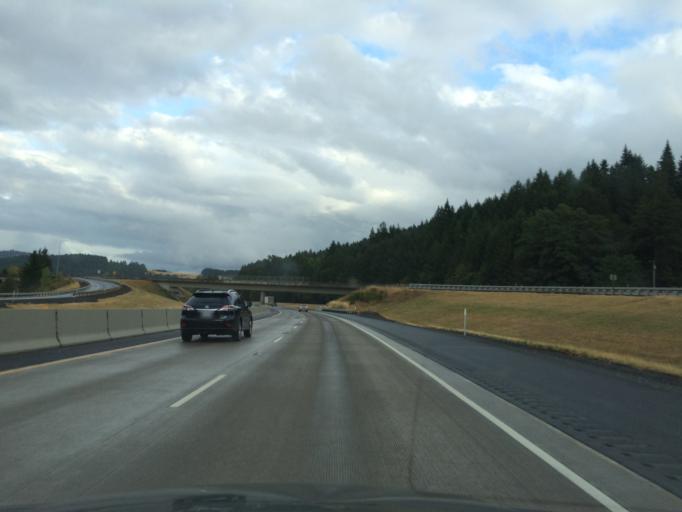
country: US
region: Oregon
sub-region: Lane County
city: Cottage Grove
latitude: 43.7507
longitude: -123.1267
